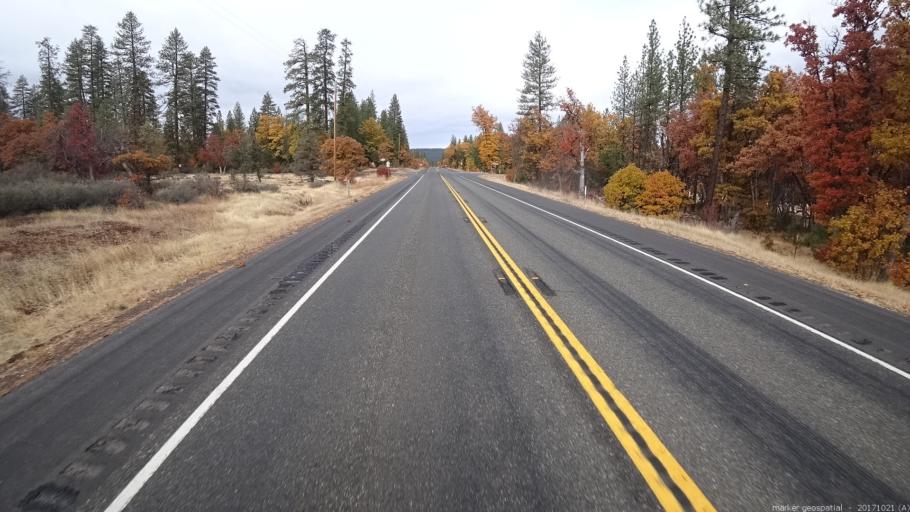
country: US
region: California
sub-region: Shasta County
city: Burney
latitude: 41.0501
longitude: -121.6372
